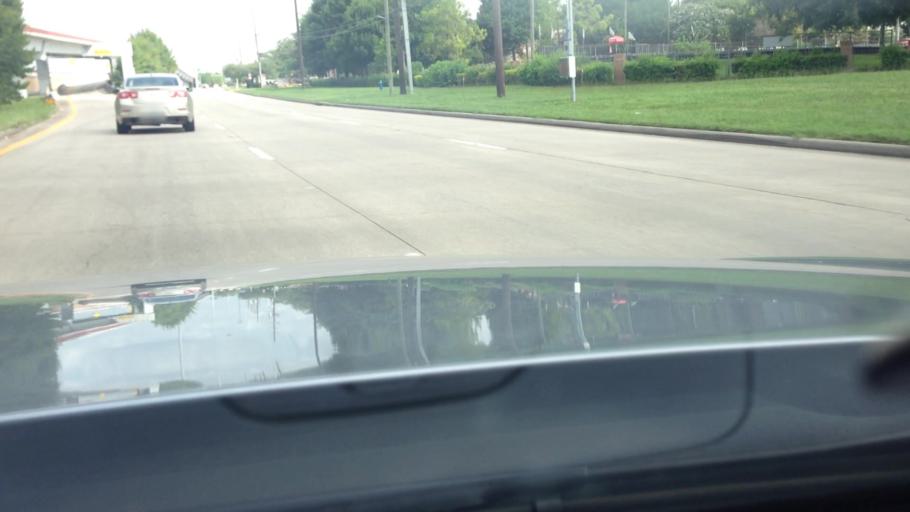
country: US
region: Texas
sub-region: Harris County
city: Hudson
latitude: 29.9542
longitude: -95.5383
